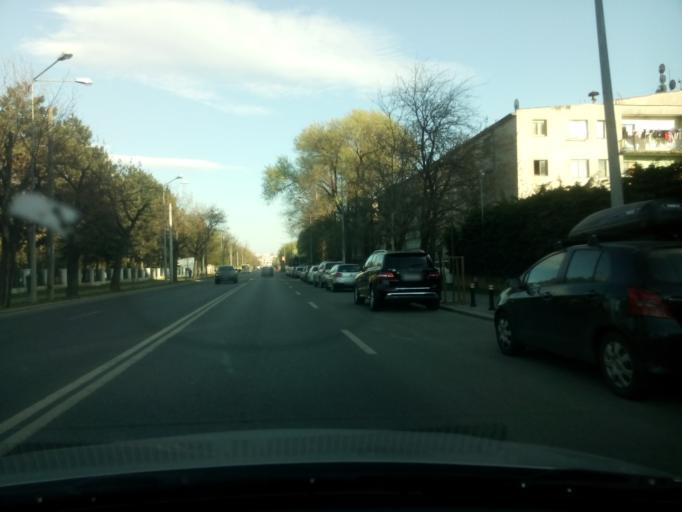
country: RO
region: Ilfov
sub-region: Comuna Otopeni
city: Otopeni
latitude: 44.4992
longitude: 26.0708
